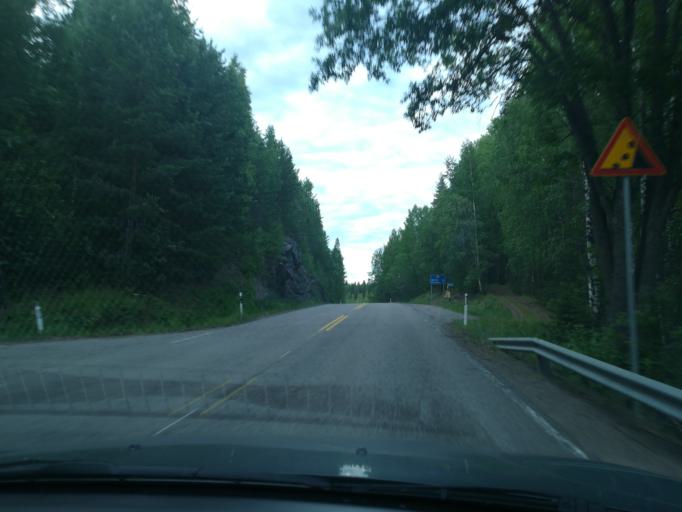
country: FI
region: Southern Savonia
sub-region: Mikkeli
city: Puumala
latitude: 61.5559
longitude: 27.9656
